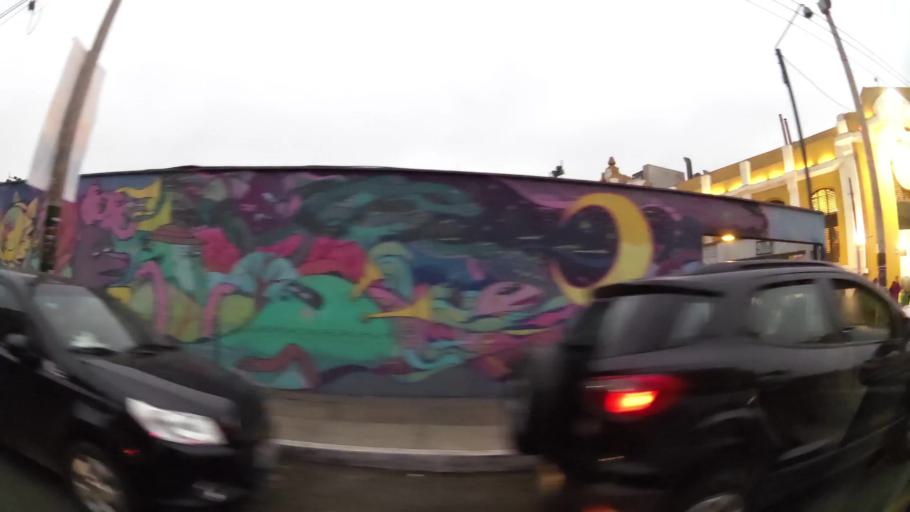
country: PE
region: Lima
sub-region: Lima
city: Surco
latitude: -12.1467
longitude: -77.0217
